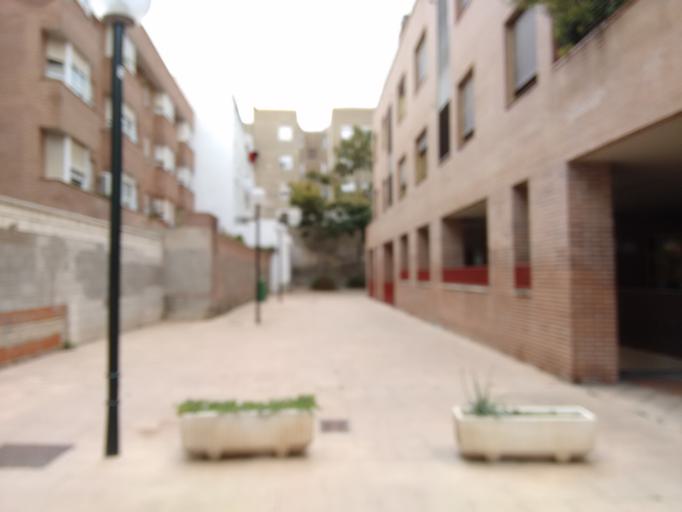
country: ES
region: Aragon
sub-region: Provincia de Zaragoza
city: Zaragoza
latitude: 41.6394
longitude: -0.8781
